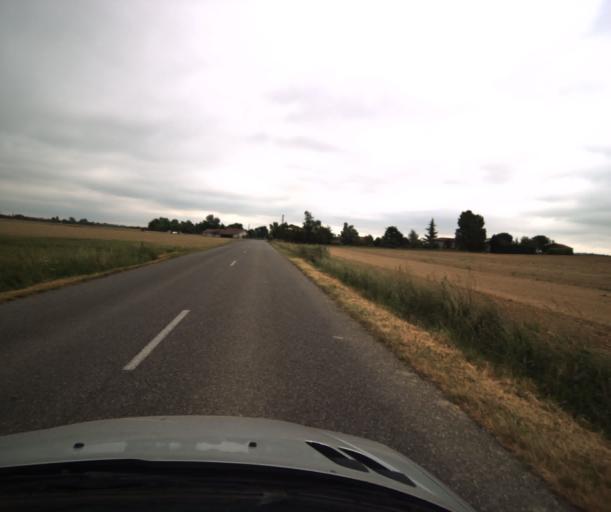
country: FR
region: Midi-Pyrenees
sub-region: Departement du Tarn-et-Garonne
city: Saint-Nicolas-de-la-Grave
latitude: 44.0331
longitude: 1.0247
